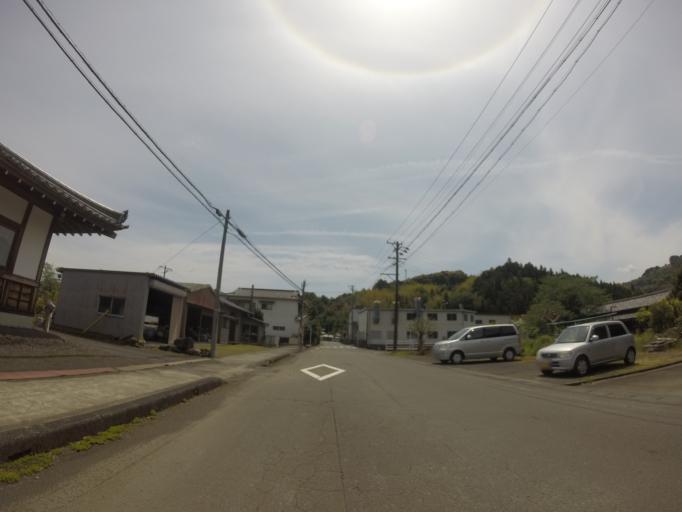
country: JP
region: Shizuoka
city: Fujieda
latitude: 34.9221
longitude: 138.2360
